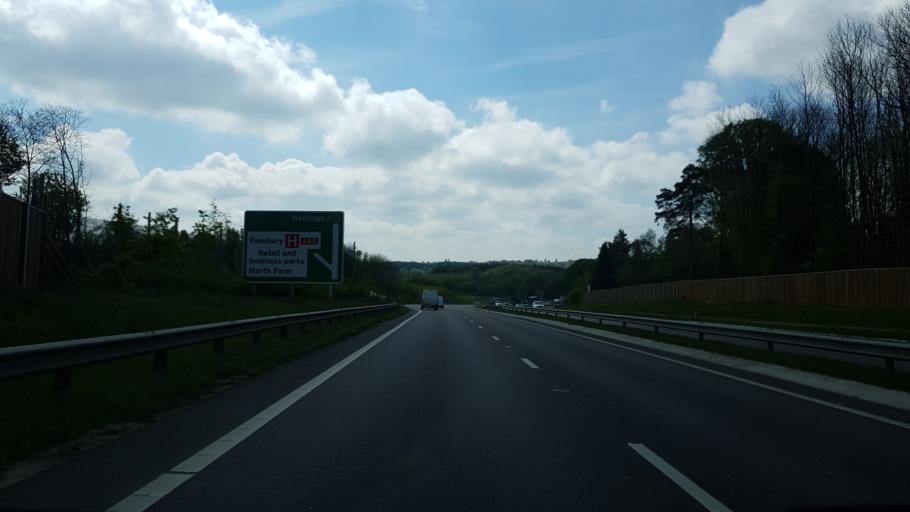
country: GB
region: England
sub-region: Kent
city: Pembury
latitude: 51.1636
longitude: 0.3062
